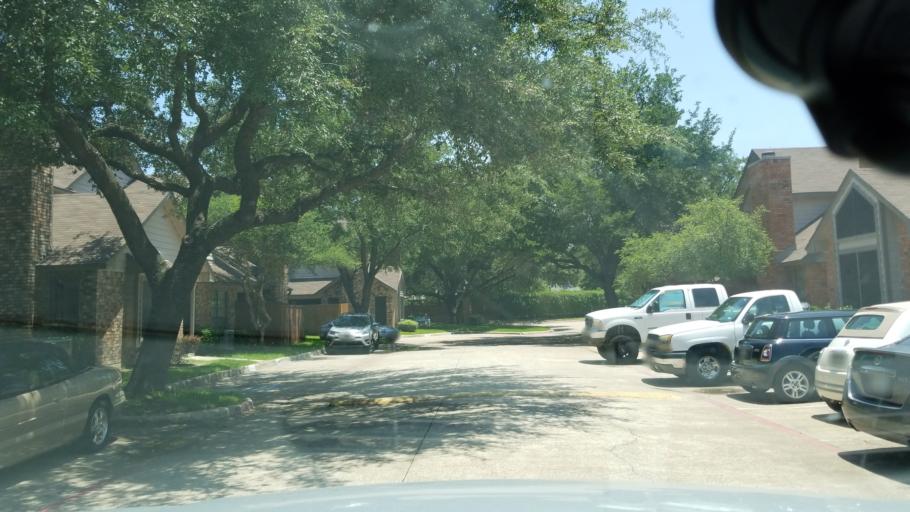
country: US
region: Texas
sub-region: Dallas County
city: Coppell
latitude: 32.9613
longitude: -96.9987
